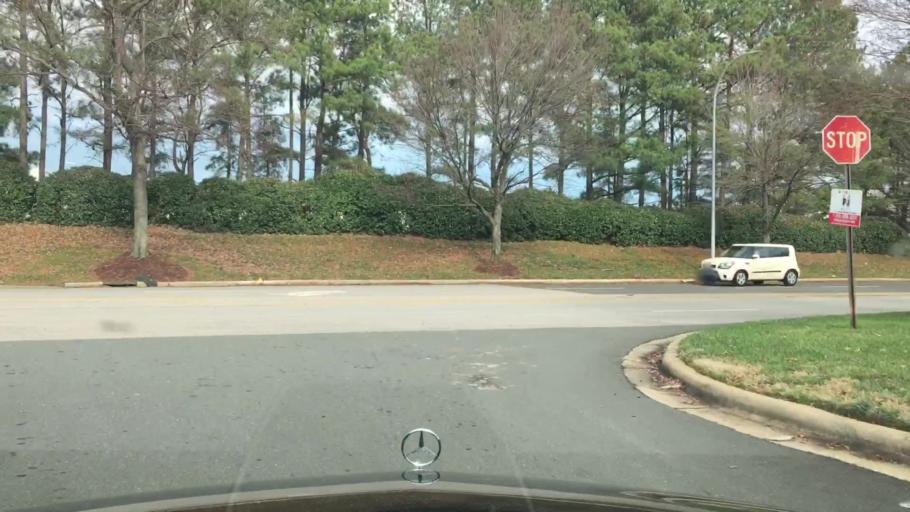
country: US
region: North Carolina
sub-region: Wake County
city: Cary
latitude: 35.7588
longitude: -78.7396
